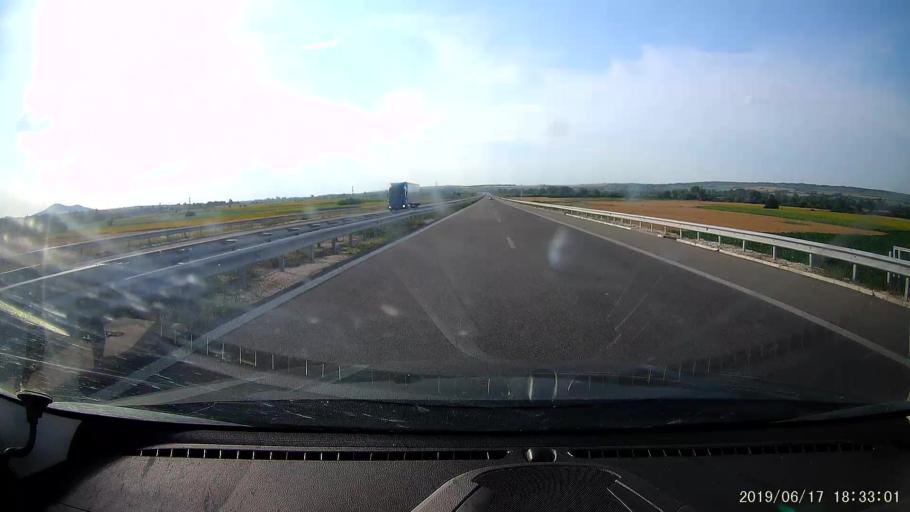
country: BG
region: Khaskovo
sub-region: Obshtina Dimitrovgrad
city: Dimitrovgrad
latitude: 42.0706
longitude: 25.4668
